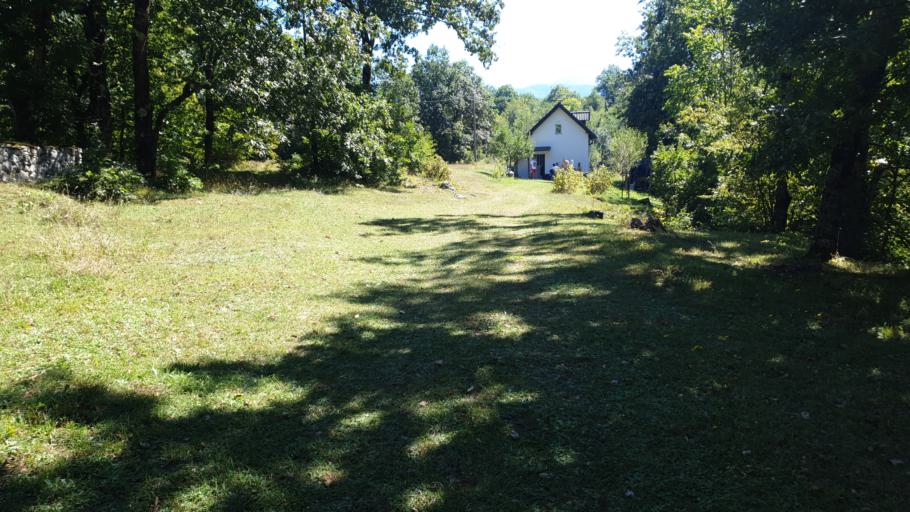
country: BA
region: Federation of Bosnia and Herzegovina
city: Polje-Bijela
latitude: 43.5249
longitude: 18.0819
